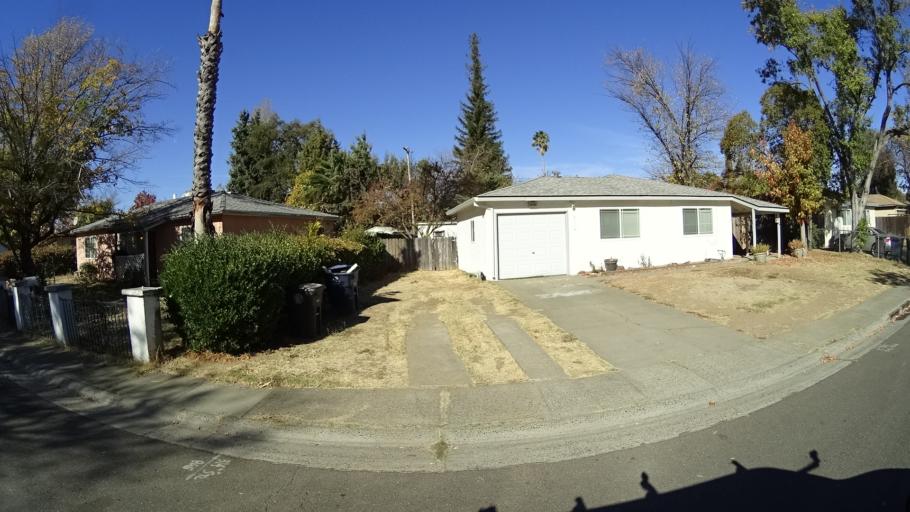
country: US
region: California
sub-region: Sacramento County
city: Antelope
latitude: 38.7158
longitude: -121.3134
